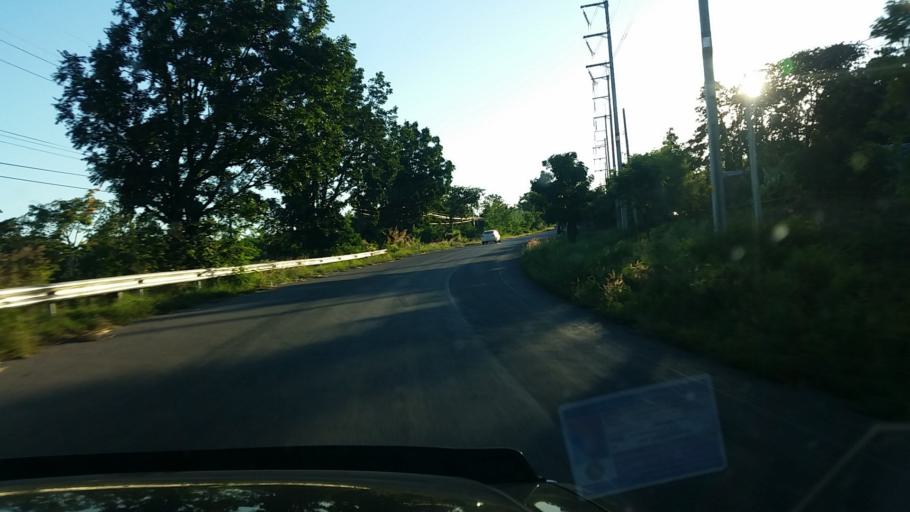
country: TH
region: Chaiyaphum
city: Sap Yai
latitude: 15.6696
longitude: 101.6737
